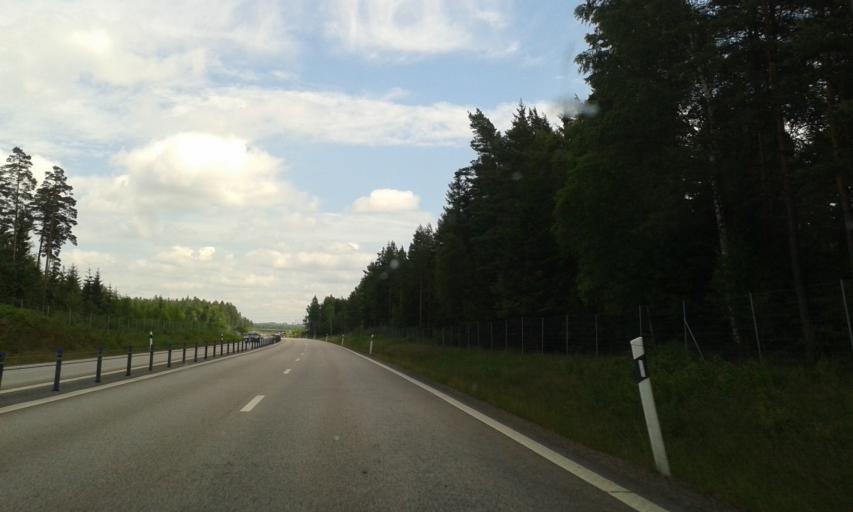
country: SE
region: Kronoberg
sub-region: Alvesta Kommun
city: Alvesta
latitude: 56.9158
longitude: 14.5106
